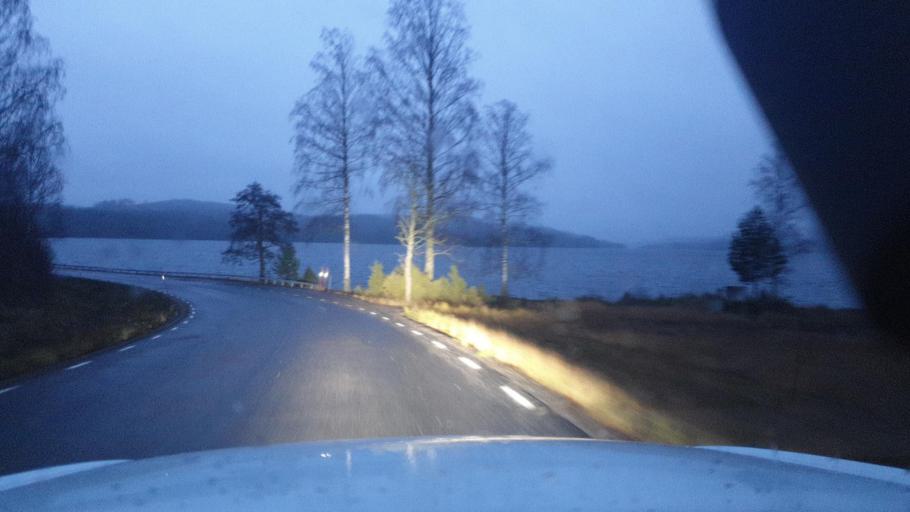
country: SE
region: Vaermland
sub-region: Torsby Kommun
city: Torsby
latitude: 59.9820
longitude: 12.7901
